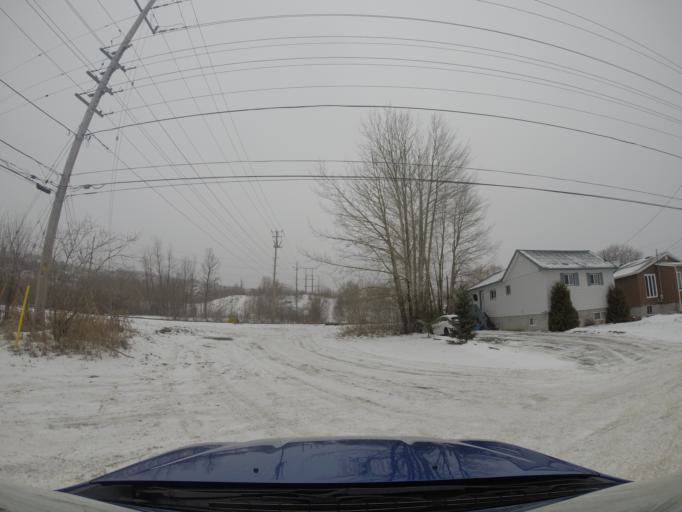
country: CA
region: Ontario
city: Greater Sudbury
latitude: 46.5043
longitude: -80.9806
